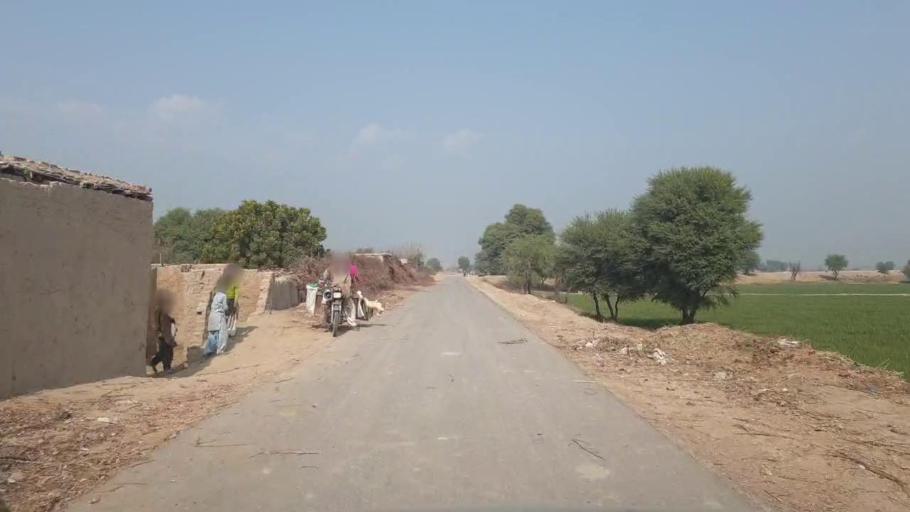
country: PK
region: Sindh
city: Hala
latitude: 25.7841
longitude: 68.3998
